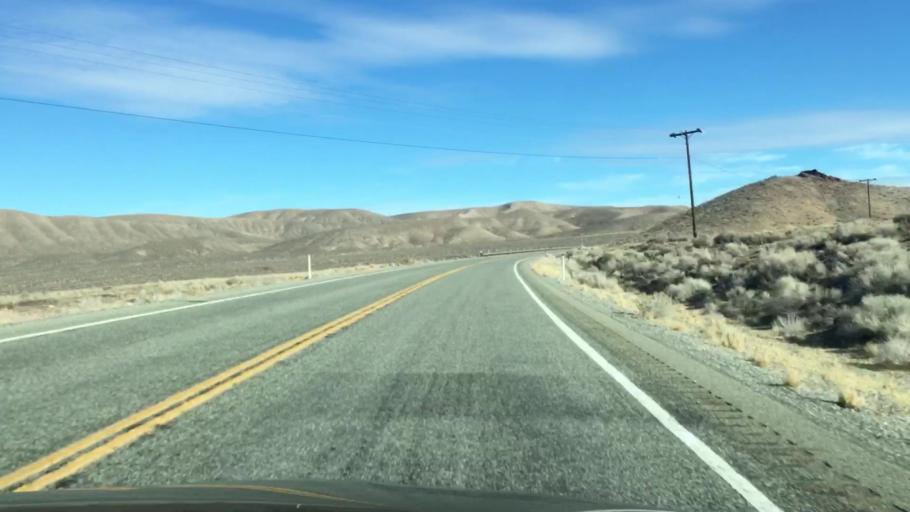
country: US
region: Nevada
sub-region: Lyon County
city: Yerington
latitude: 39.0460
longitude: -118.9741
